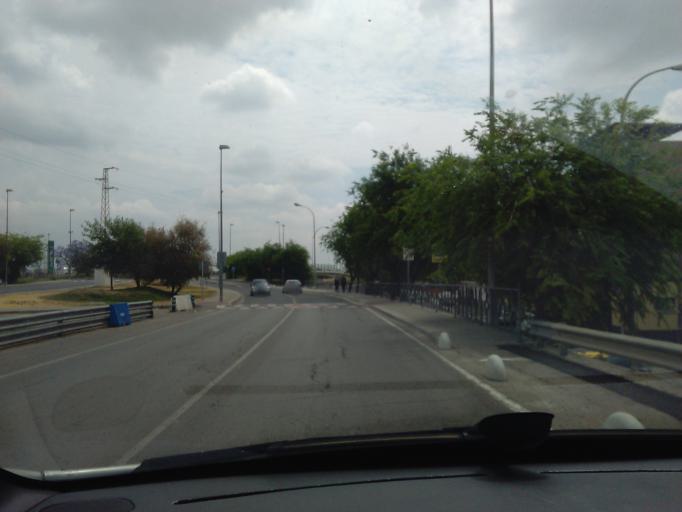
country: ES
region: Andalusia
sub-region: Provincia de Sevilla
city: Sevilla
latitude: 37.3715
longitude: -5.9409
